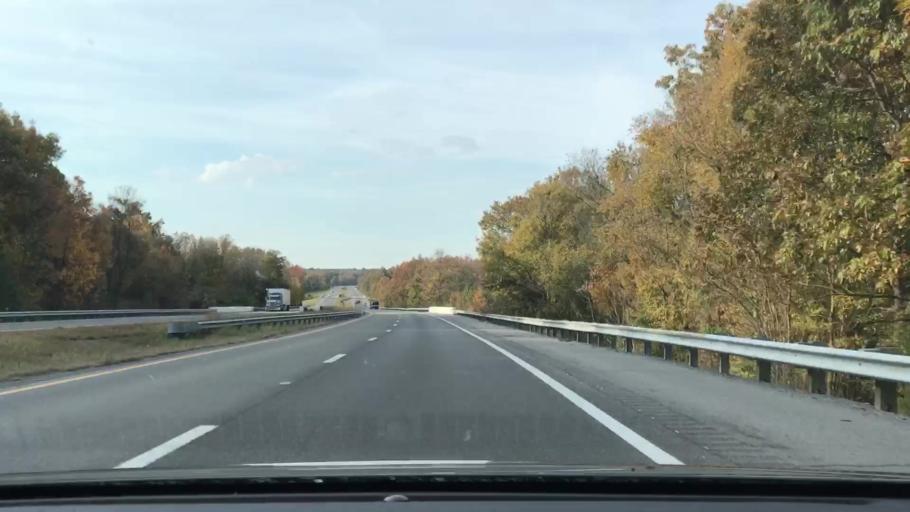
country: US
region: Kentucky
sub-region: Marshall County
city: Benton
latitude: 36.8163
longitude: -88.4859
